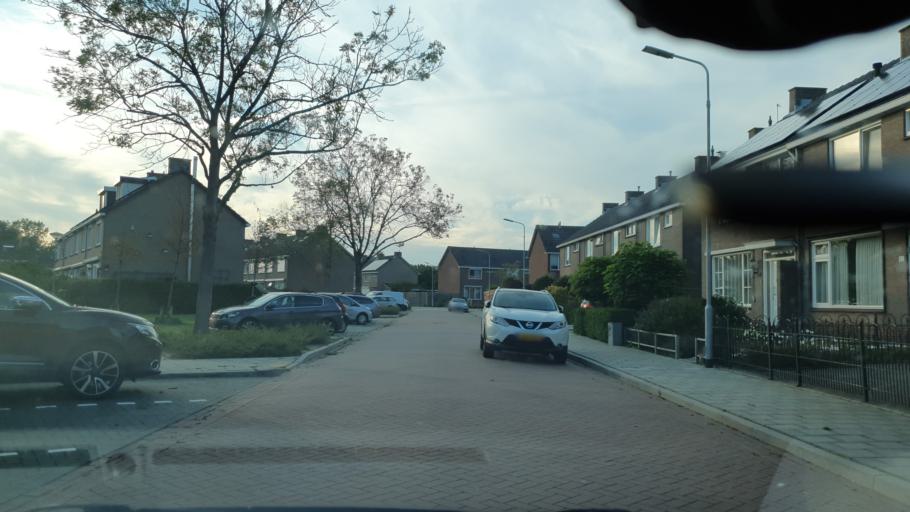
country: NL
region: Zeeland
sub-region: Gemeente Vlissingen
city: Vlissingen
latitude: 51.4598
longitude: 3.5967
